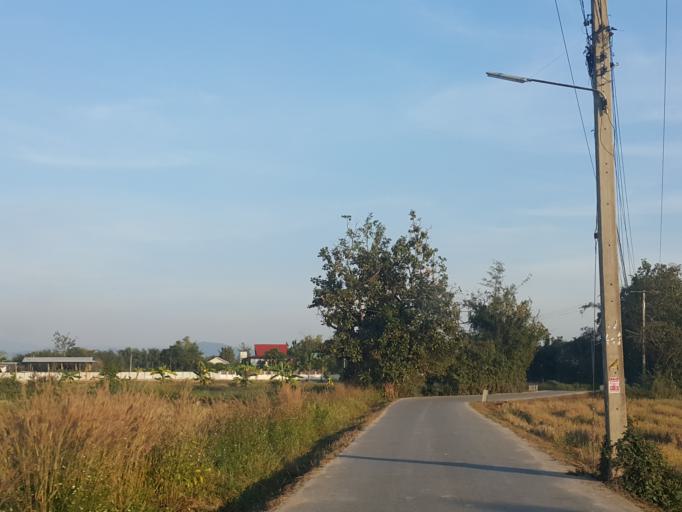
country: TH
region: Chiang Mai
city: San Sai
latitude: 18.8207
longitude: 99.0946
